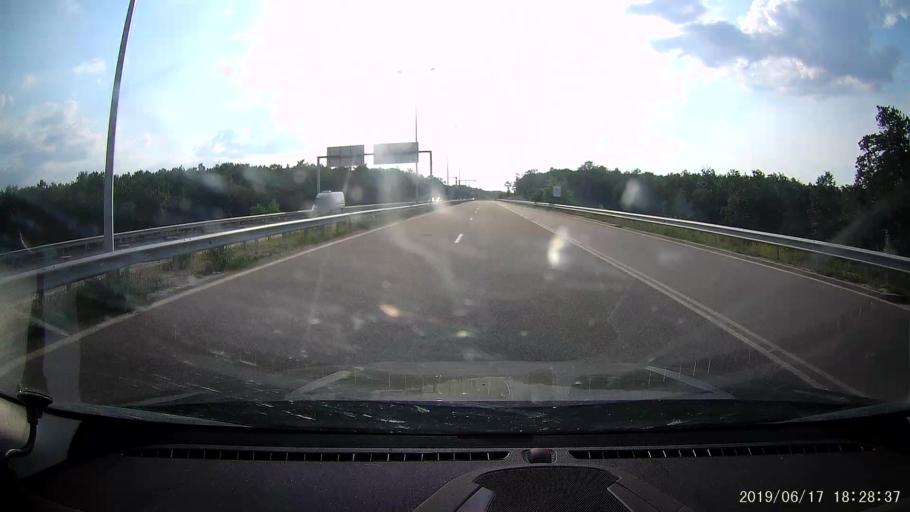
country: BG
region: Khaskovo
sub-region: Obshtina Dimitrovgrad
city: Dimitrovgrad
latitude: 42.0237
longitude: 25.5749
